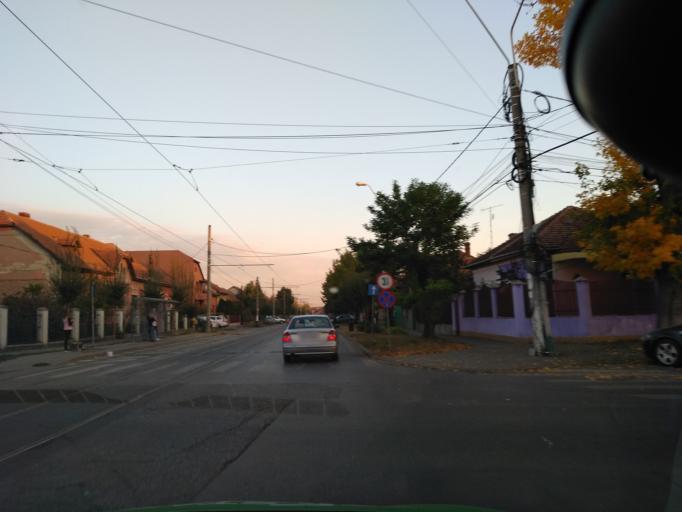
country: RO
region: Timis
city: Timisoara
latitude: 45.7321
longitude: 21.2279
